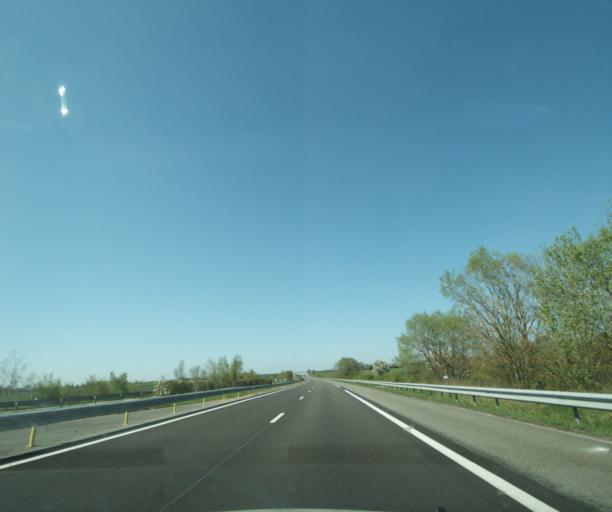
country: FR
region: Bourgogne
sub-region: Departement de la Nievre
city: Neuvy-sur-Loire
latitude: 47.5168
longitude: 2.9161
